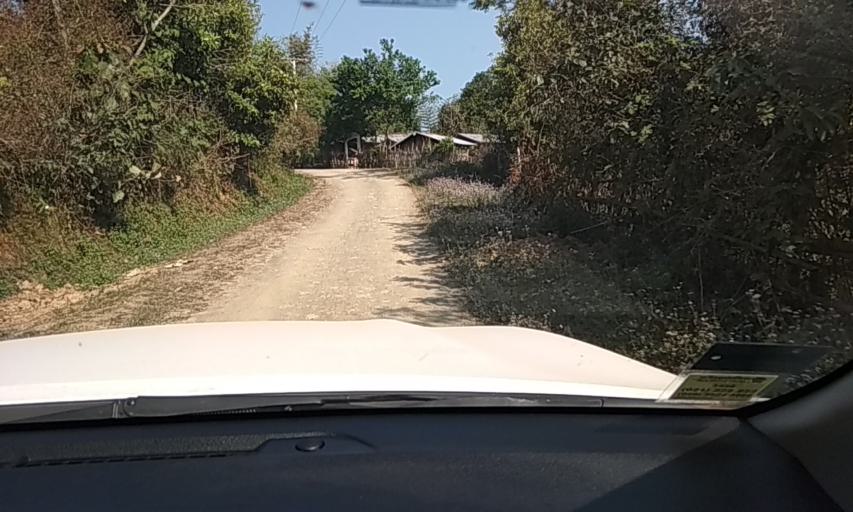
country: LA
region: Phongsali
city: Phongsali
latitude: 21.6977
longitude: 102.0820
